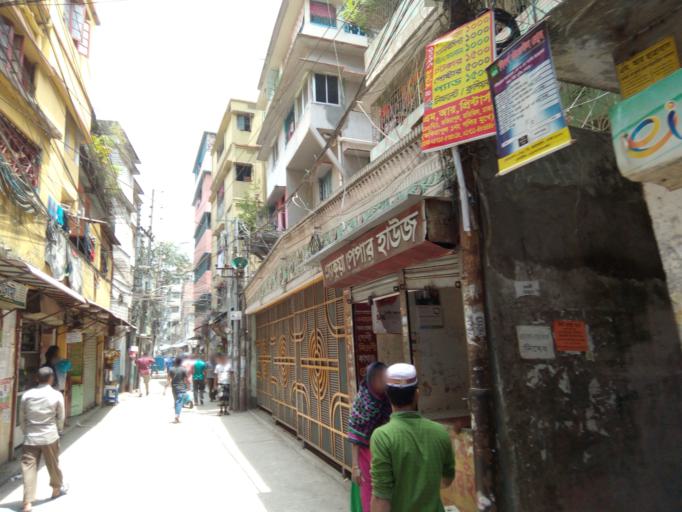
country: BD
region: Dhaka
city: Paltan
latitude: 23.7308
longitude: 90.4196
